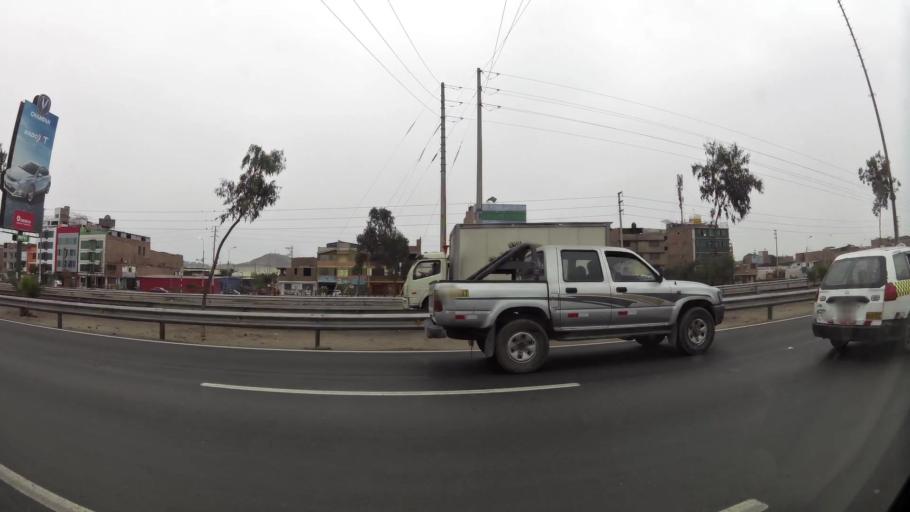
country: PE
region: Lima
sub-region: Lima
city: Surco
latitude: -12.1770
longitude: -76.9771
